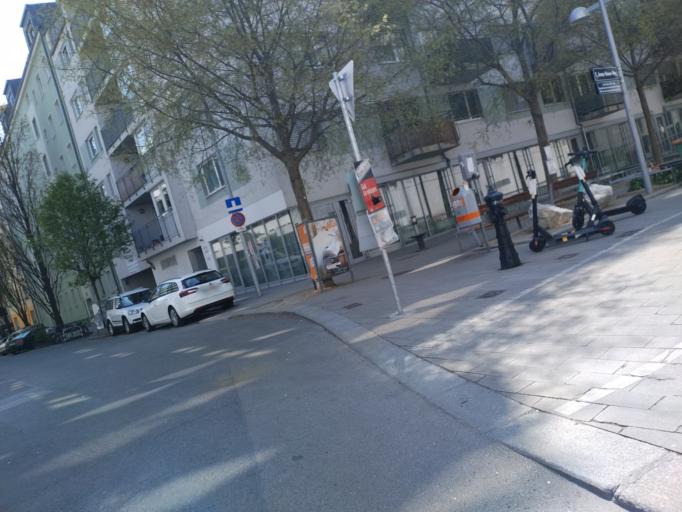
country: AT
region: Vienna
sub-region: Wien Stadt
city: Vienna
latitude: 48.2004
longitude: 16.3469
